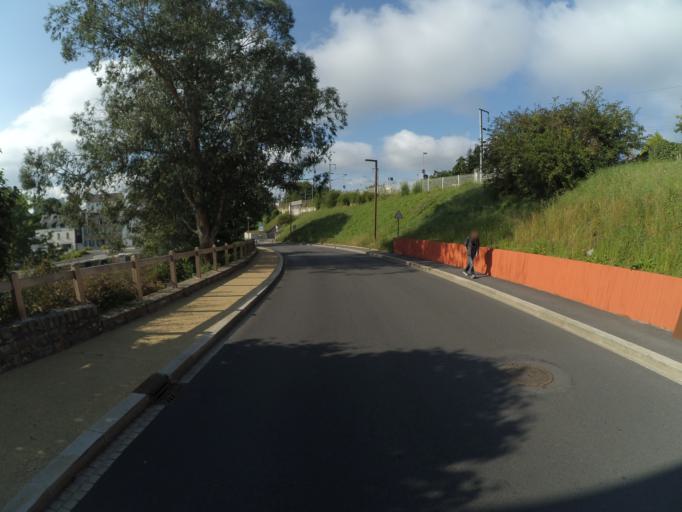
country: FR
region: Brittany
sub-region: Departement du Finistere
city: Quimperle
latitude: 47.8689
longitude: -3.5525
